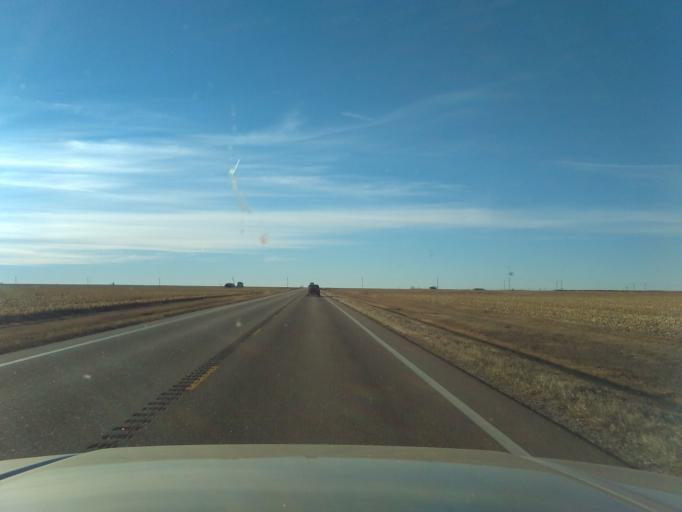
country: US
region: Kansas
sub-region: Thomas County
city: Colby
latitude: 39.4649
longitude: -100.7502
